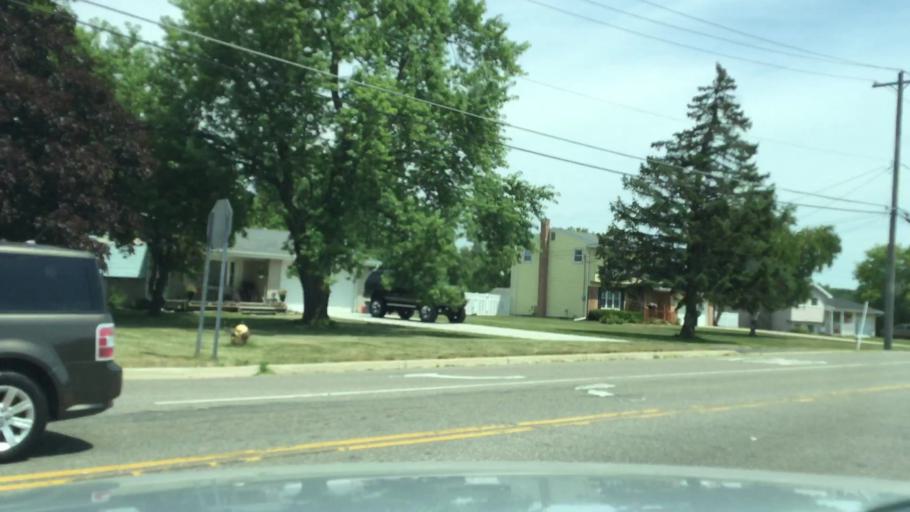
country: US
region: Michigan
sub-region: Genesee County
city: Flushing
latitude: 43.0159
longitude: -83.8122
